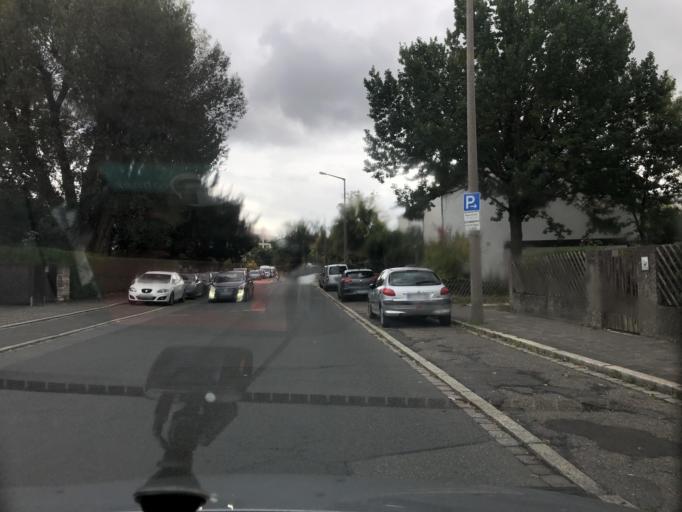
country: DE
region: Bavaria
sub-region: Regierungsbezirk Mittelfranken
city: Nuernberg
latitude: 49.4652
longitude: 11.0639
